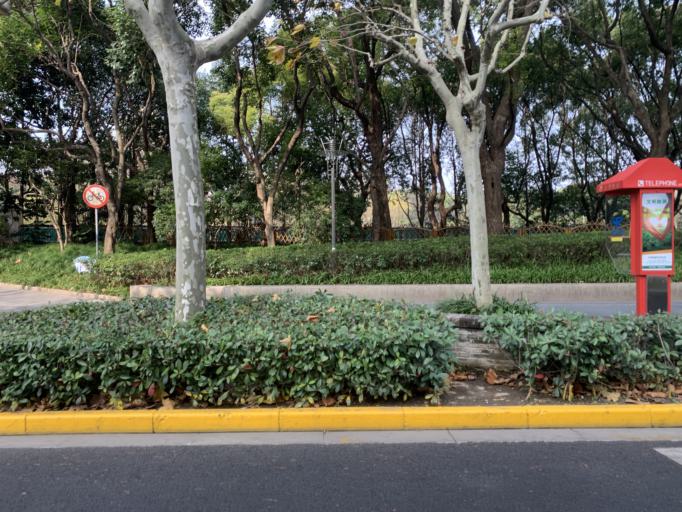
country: CN
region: Shanghai Shi
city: Xuhui
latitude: 31.1979
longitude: 121.4376
